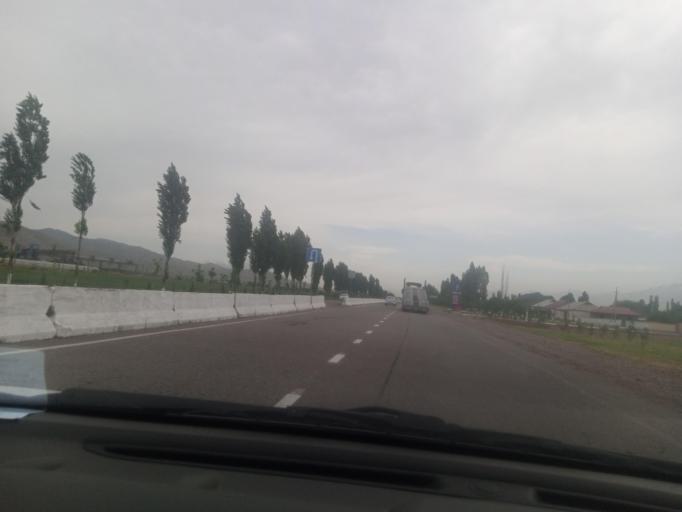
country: UZ
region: Toshkent
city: Ohangaron
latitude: 40.9105
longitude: 69.8119
